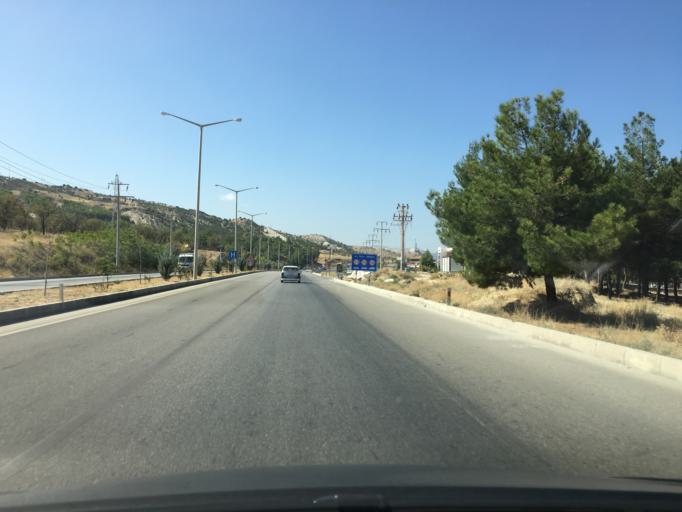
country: TR
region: Burdur
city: Burdur
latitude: 37.7541
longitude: 30.3348
